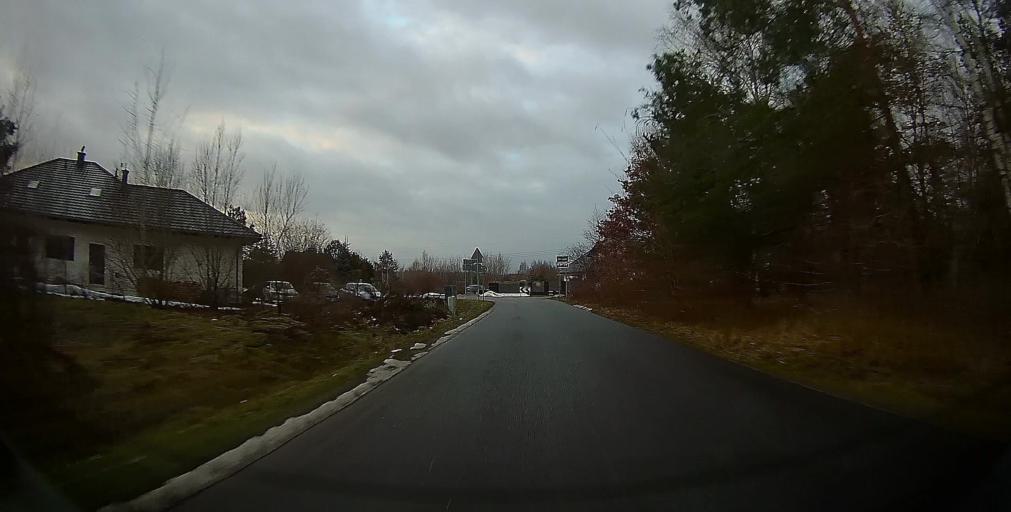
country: PL
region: Masovian Voivodeship
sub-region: Radom
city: Radom
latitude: 51.4540
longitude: 21.1271
